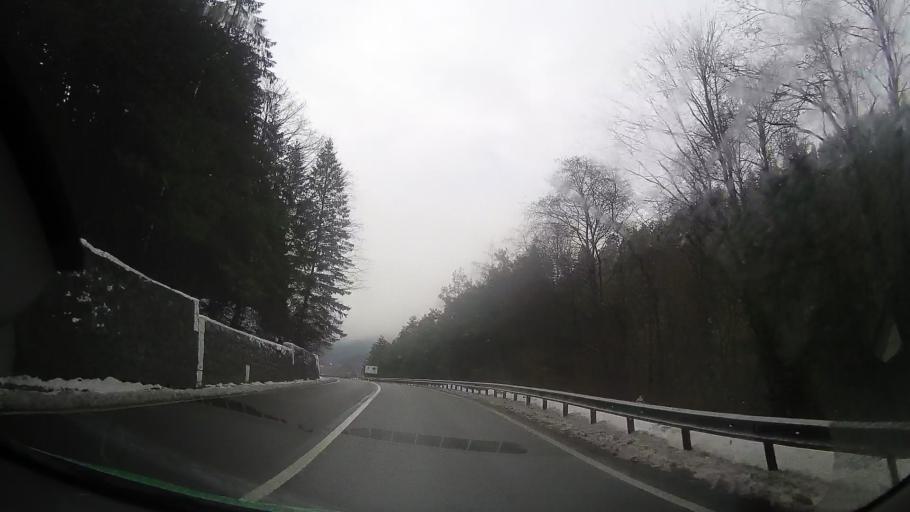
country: RO
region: Neamt
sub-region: Comuna Tasca
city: Tasca
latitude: 46.8963
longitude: 26.0454
